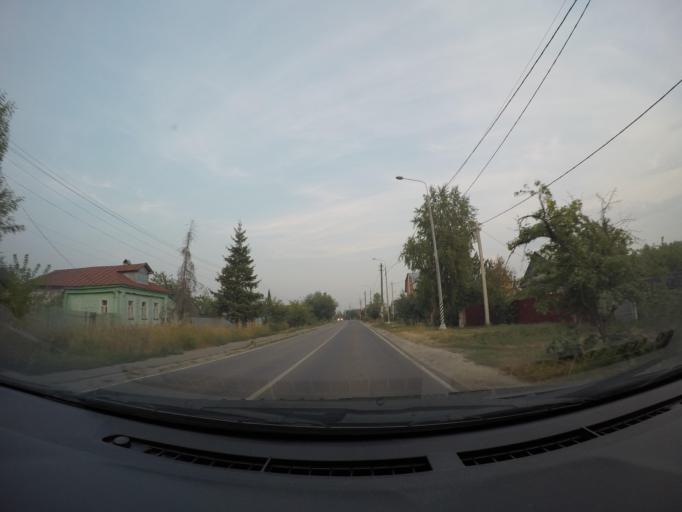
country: RU
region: Moskovskaya
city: Imeni Tsyurupy
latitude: 55.4931
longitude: 38.6653
